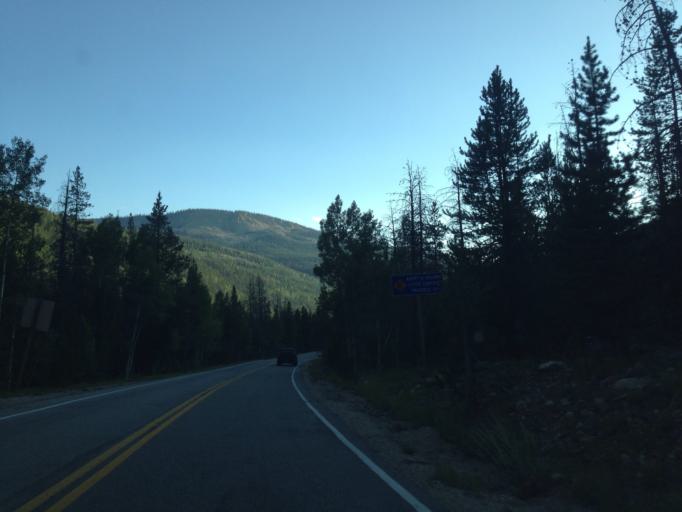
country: US
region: Utah
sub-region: Summit County
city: Francis
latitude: 40.6063
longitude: -110.9626
